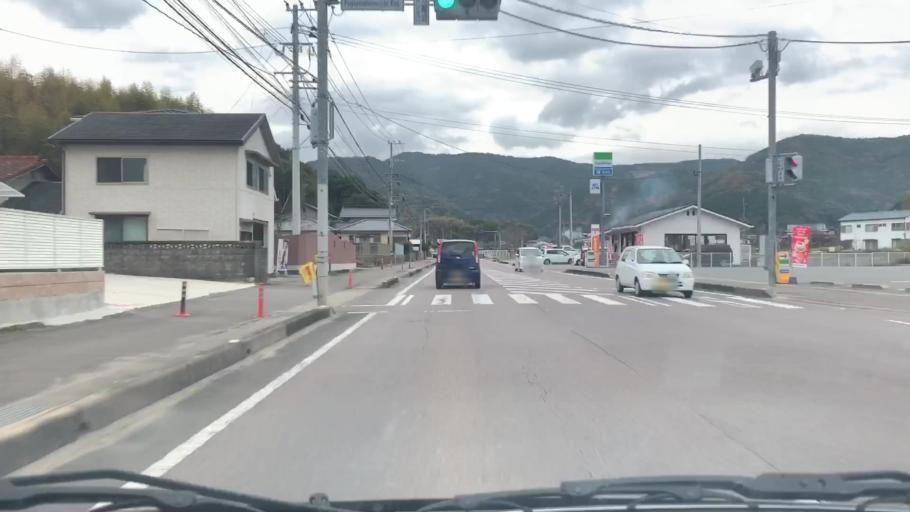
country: JP
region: Saga Prefecture
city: Kashima
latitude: 33.1498
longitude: 130.0636
